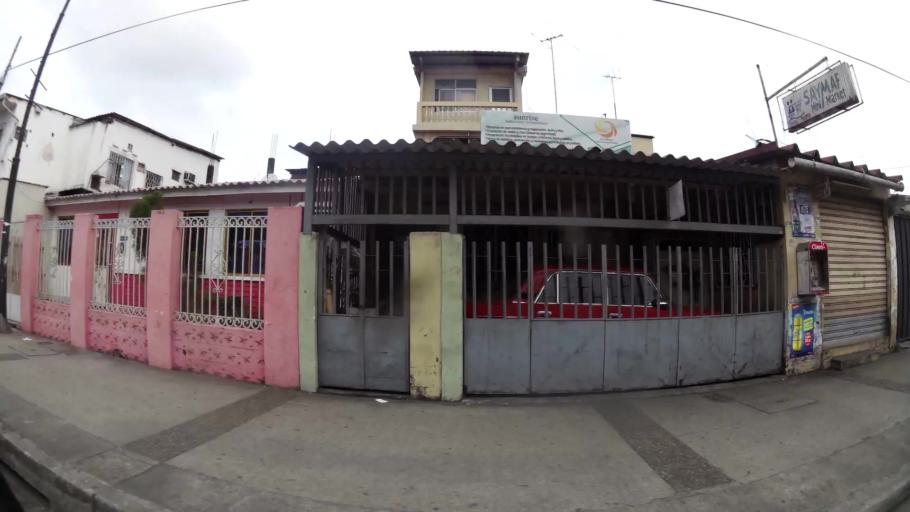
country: EC
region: Guayas
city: Eloy Alfaro
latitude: -2.1713
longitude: -79.8798
